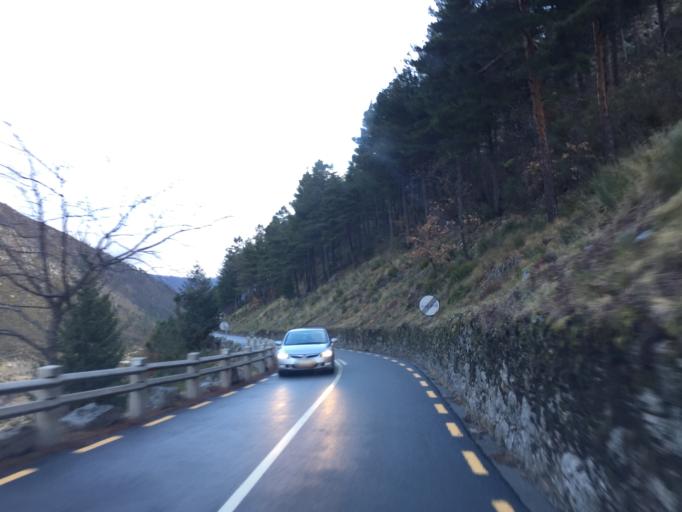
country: PT
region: Guarda
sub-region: Manteigas
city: Manteigas
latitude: 40.3503
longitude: -7.5602
